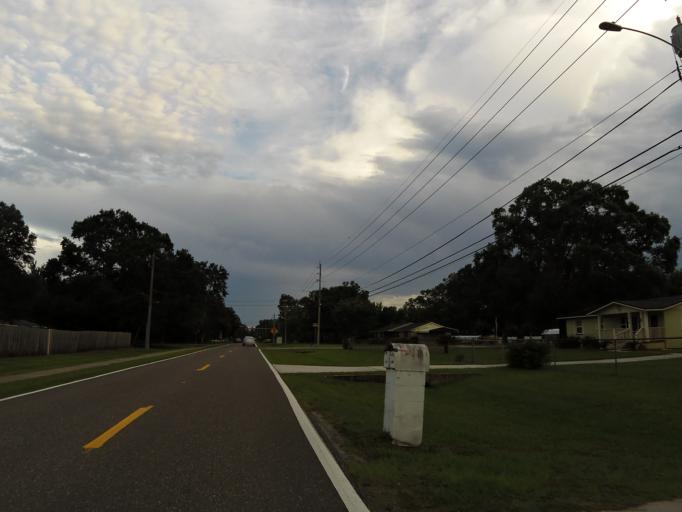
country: US
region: Florida
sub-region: Duval County
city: Baldwin
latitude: 30.3040
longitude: -81.8320
